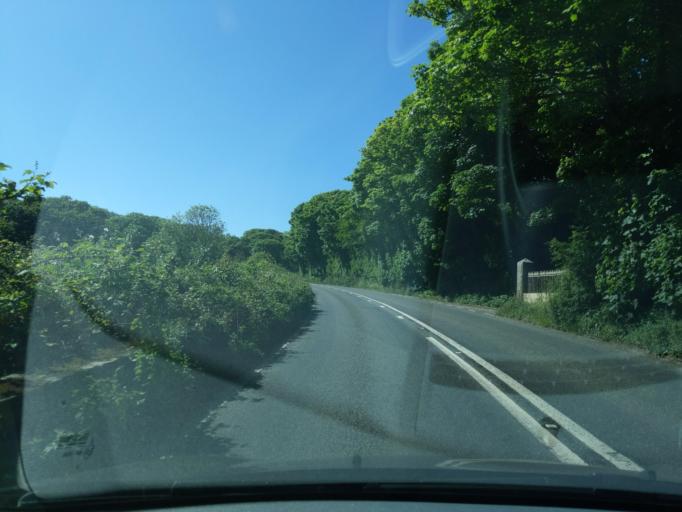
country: GB
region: England
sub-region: Cornwall
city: Porthleven
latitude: 50.1036
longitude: -5.3277
